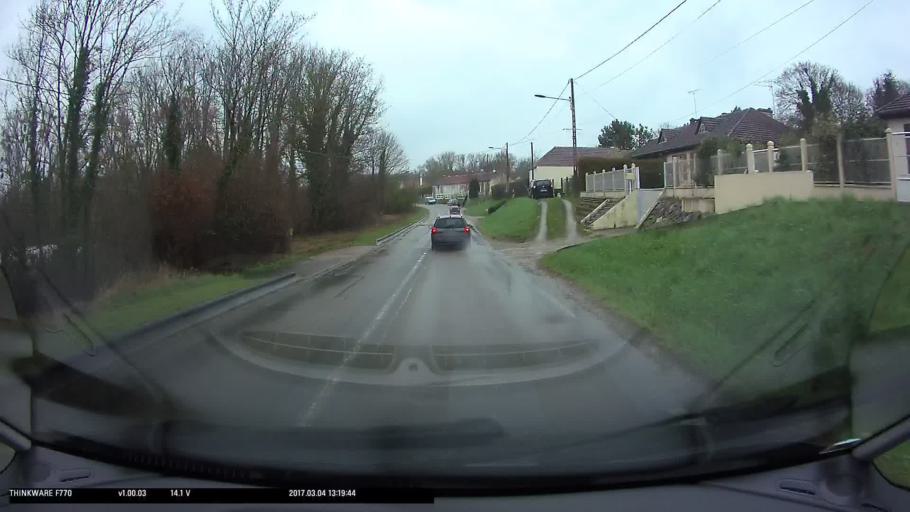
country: FR
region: Ile-de-France
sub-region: Departement du Val-d'Oise
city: Us
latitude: 49.0998
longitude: 1.9762
